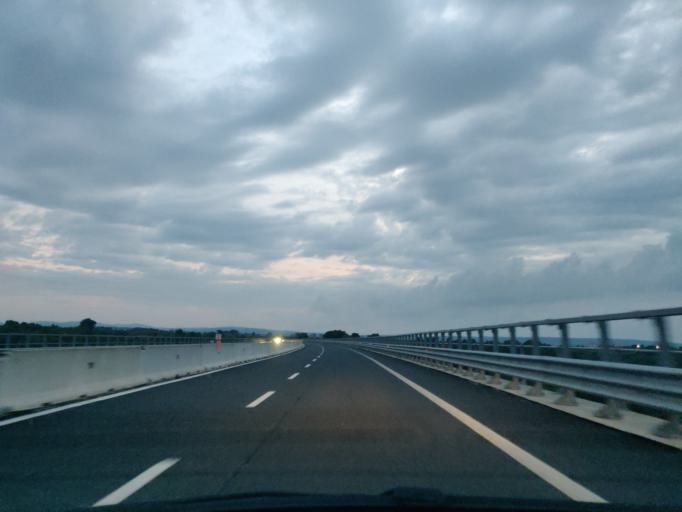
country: IT
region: Latium
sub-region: Provincia di Viterbo
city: Vetralla
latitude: 42.3604
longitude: 11.9892
